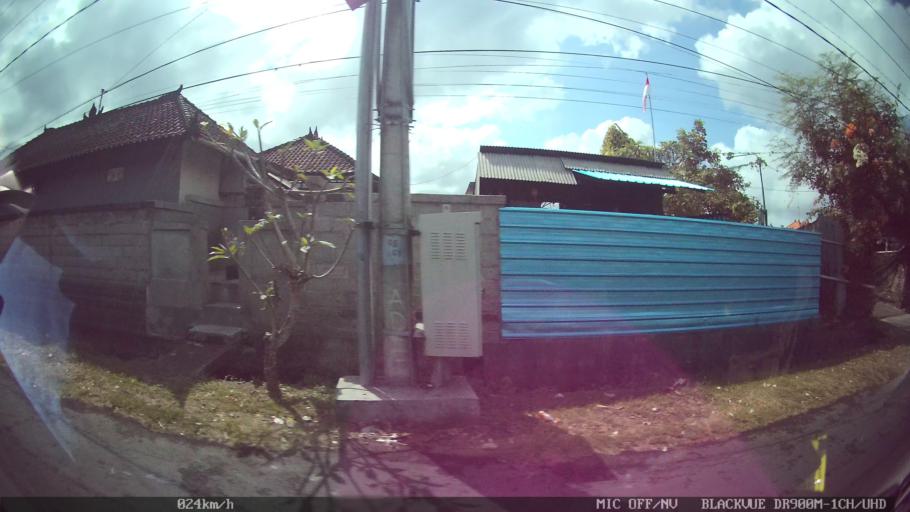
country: ID
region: Bali
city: Banjar Batur
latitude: -8.5984
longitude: 115.2048
